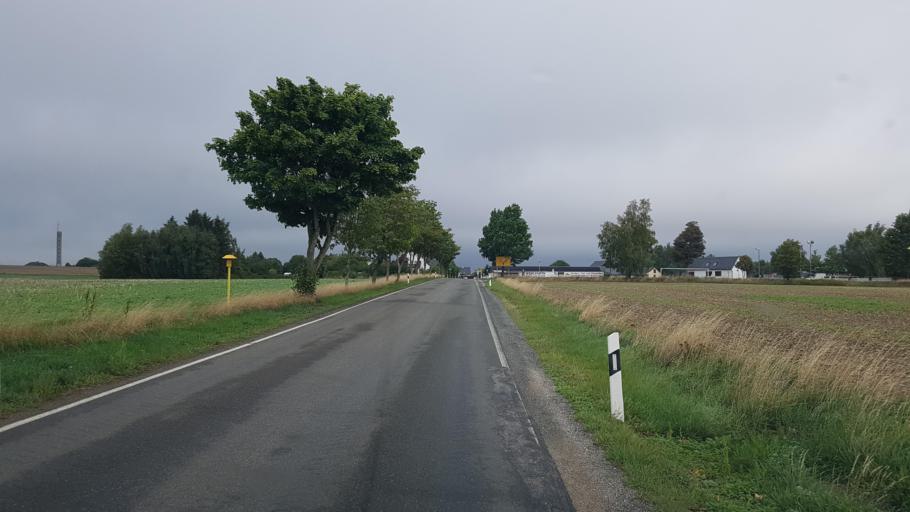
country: DE
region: Thuringia
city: Bad Lobenstein
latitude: 50.4926
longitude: 11.6042
